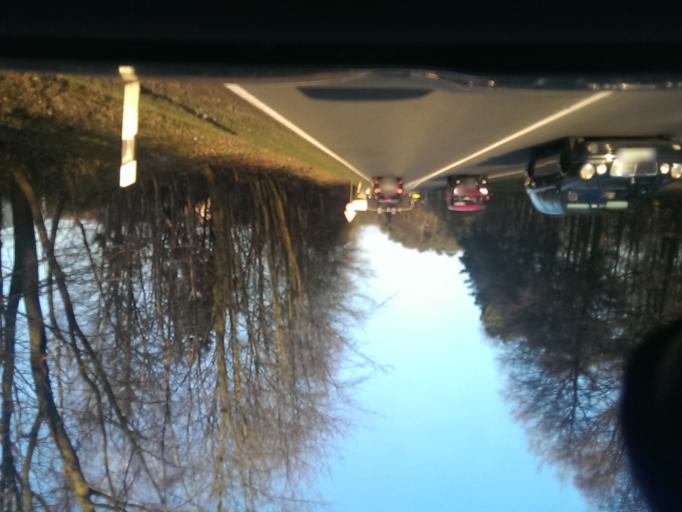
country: DE
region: North Rhine-Westphalia
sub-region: Regierungsbezirk Detmold
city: Hovelhof
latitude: 51.7854
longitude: 8.6134
